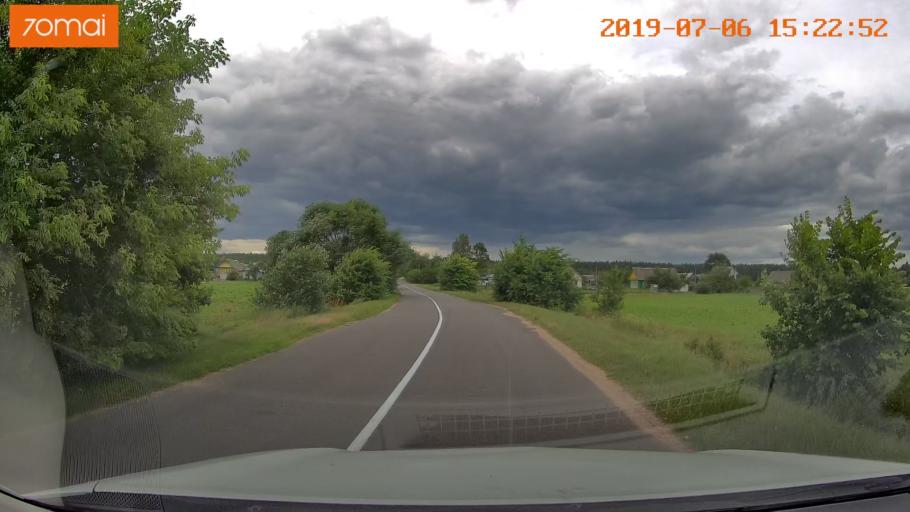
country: BY
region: Minsk
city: Valozhyn
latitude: 54.0152
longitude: 26.6051
